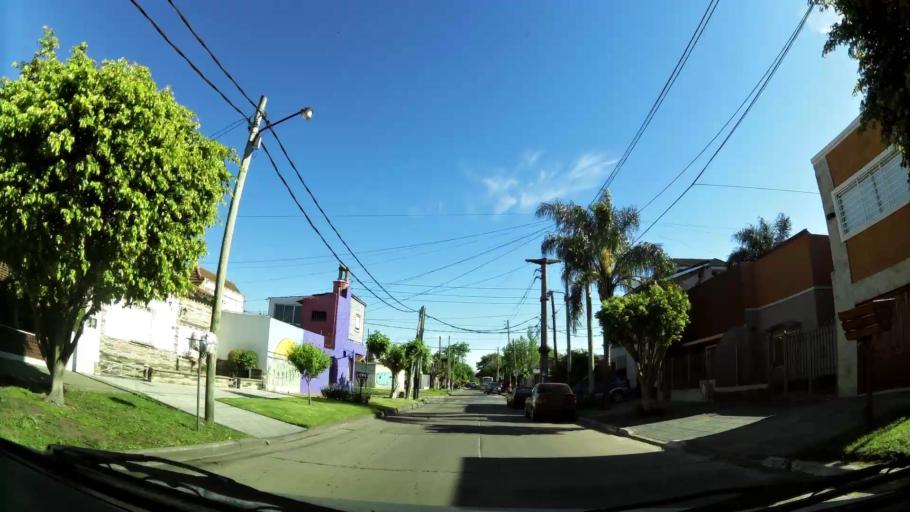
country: AR
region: Buenos Aires
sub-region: Partido de Lomas de Zamora
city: Lomas de Zamora
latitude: -34.7649
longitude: -58.4201
